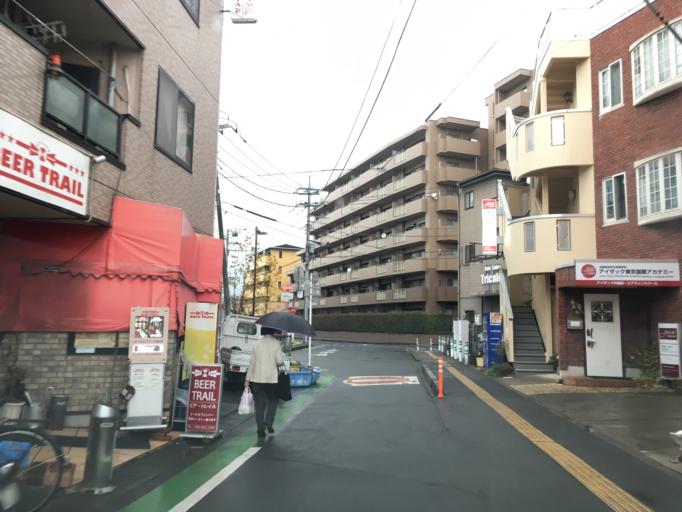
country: JP
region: Saitama
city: Koshigaya
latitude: 35.8774
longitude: 139.7917
